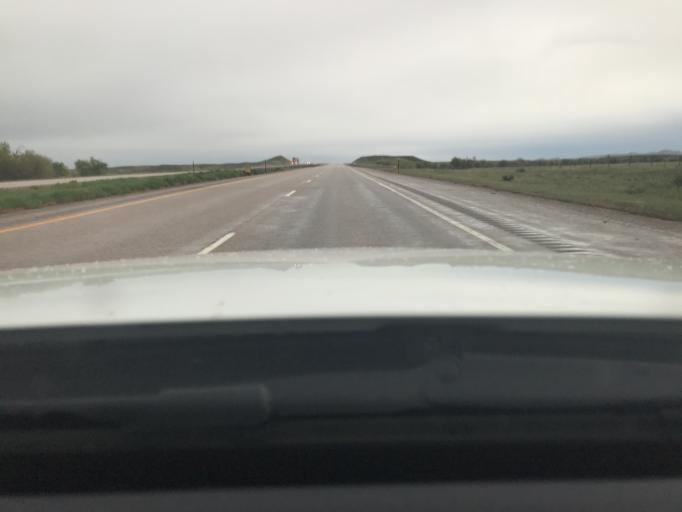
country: US
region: Wyoming
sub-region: Converse County
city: Glenrock
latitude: 42.8136
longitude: -105.6957
